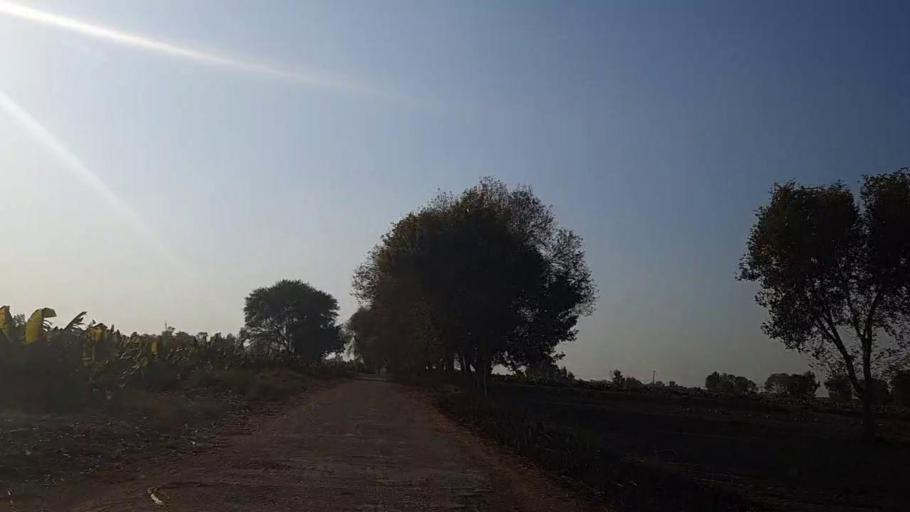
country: PK
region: Sindh
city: Daur
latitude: 26.3327
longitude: 68.1476
